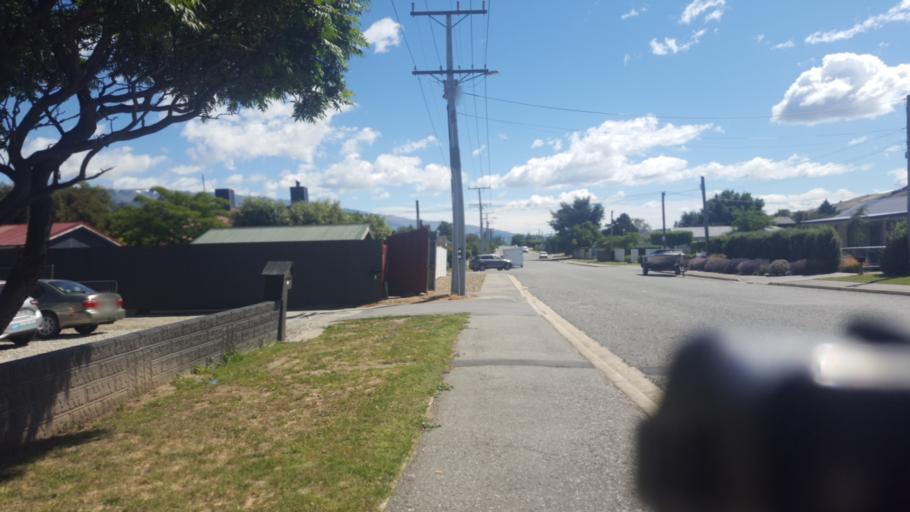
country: NZ
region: Otago
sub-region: Queenstown-Lakes District
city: Wanaka
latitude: -45.0461
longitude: 169.2105
